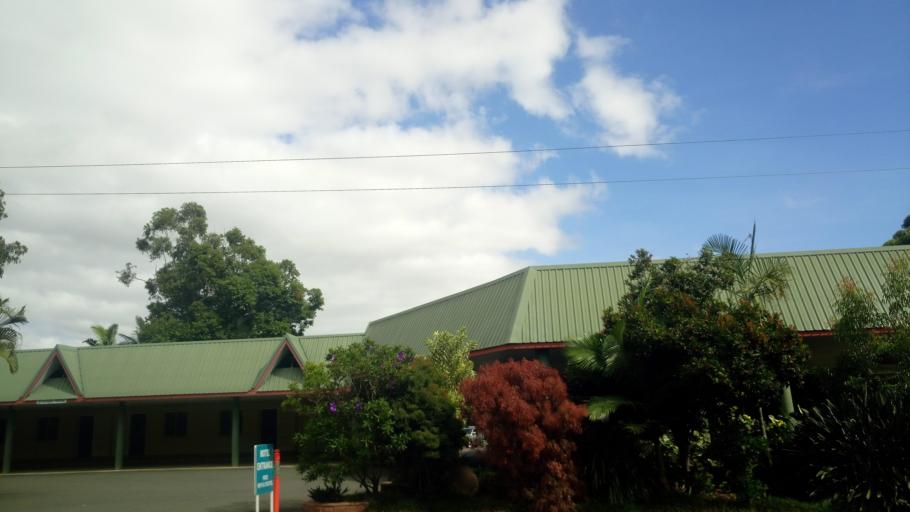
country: AU
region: Queensland
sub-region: Tablelands
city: Mareeba
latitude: -17.0100
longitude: 145.4248
